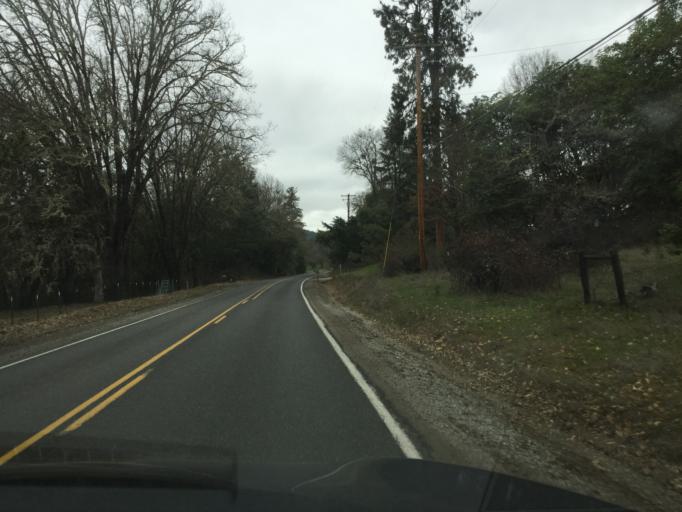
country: US
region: Oregon
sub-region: Jackson County
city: Gold Hill
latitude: 42.4033
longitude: -123.0273
